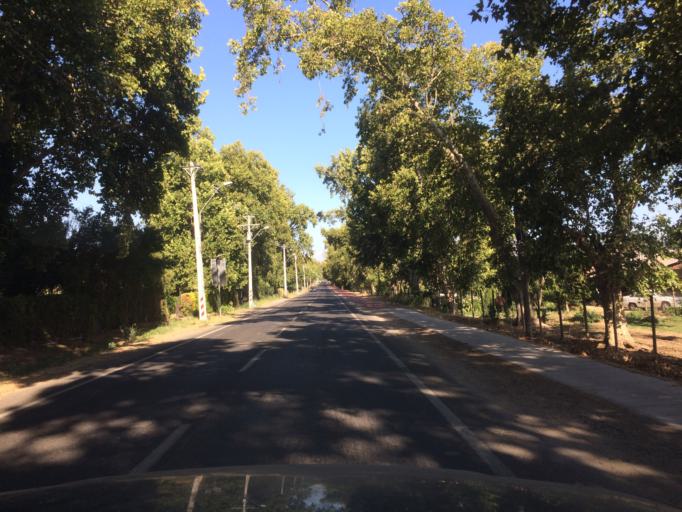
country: CL
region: Santiago Metropolitan
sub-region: Provincia de Melipilla
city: Melipilla
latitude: -33.4896
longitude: -71.1790
